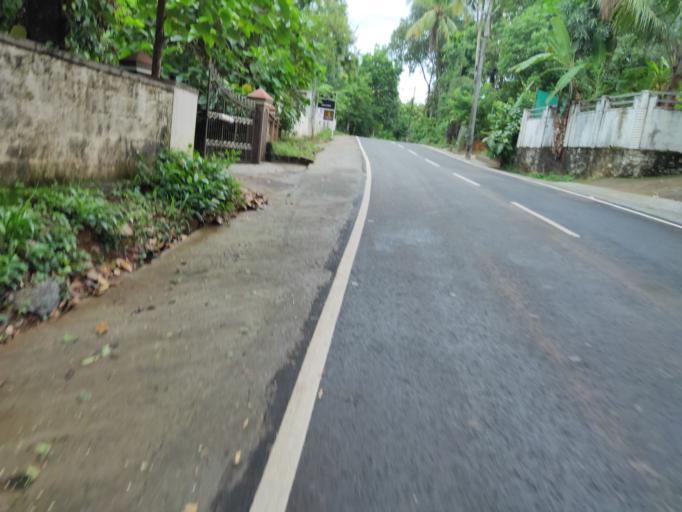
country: IN
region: Kerala
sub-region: Malappuram
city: Manjeri
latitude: 11.1858
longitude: 76.2083
